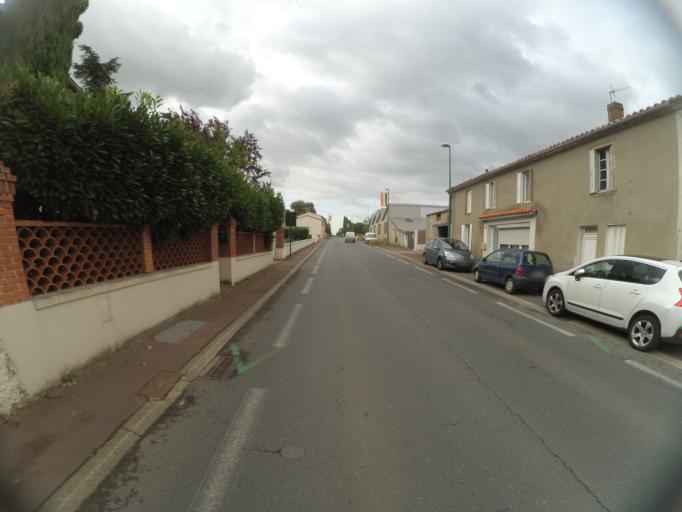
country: FR
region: Pays de la Loire
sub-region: Departement de la Vendee
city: Cugand
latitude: 47.0620
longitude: -1.2565
